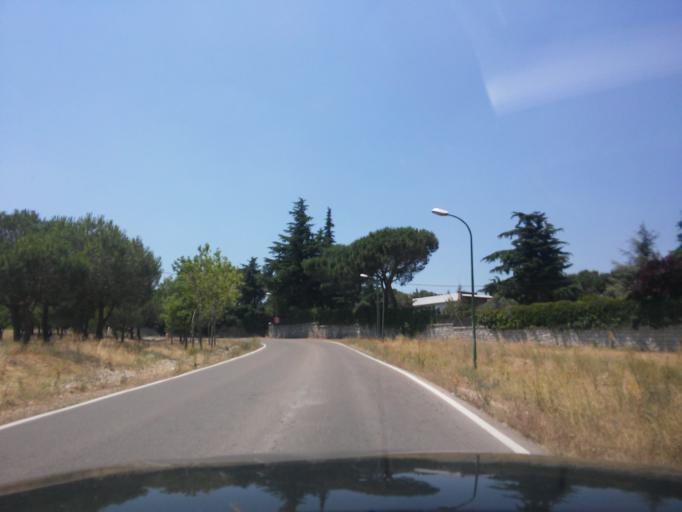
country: ES
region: Madrid
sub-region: Provincia de Madrid
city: Collado-Villalba
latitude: 40.6274
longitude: -4.0299
